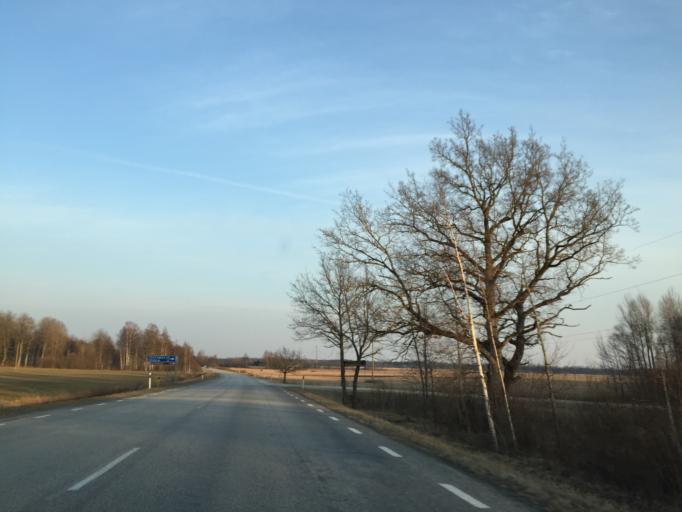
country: EE
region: Laeaene
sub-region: Lihula vald
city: Lihula
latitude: 58.5393
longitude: 24.0123
